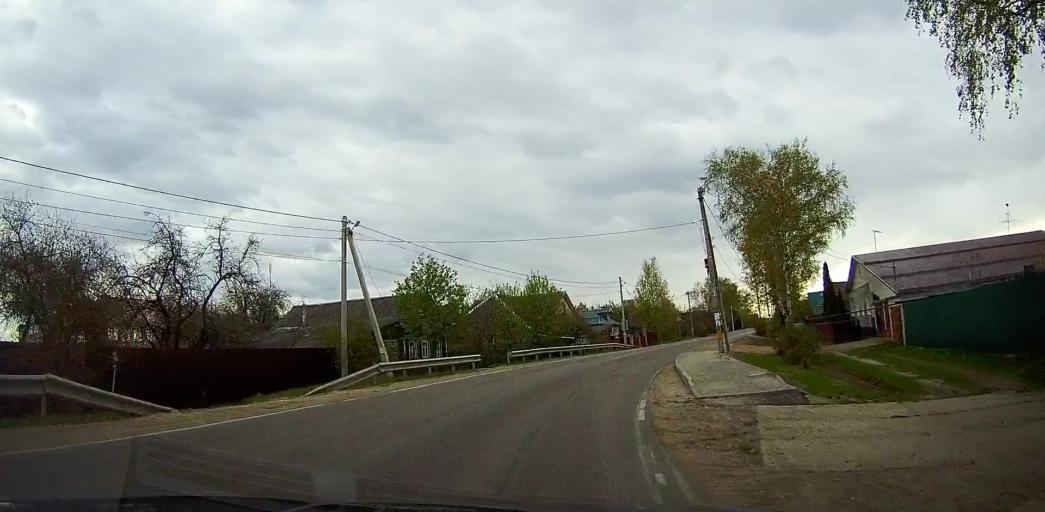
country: RU
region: Moskovskaya
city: Pavlovskiy Posad
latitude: 55.7578
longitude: 38.7083
